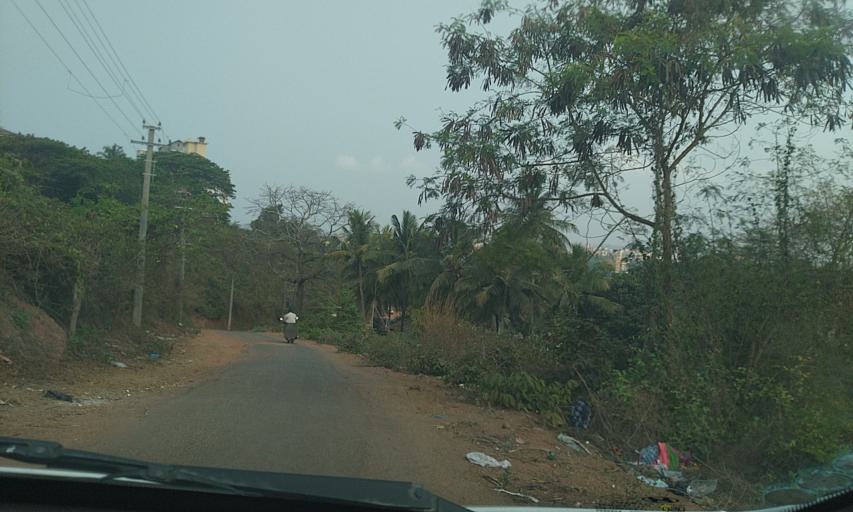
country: IN
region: Goa
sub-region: North Goa
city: Taleigao
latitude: 15.4630
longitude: 73.8167
